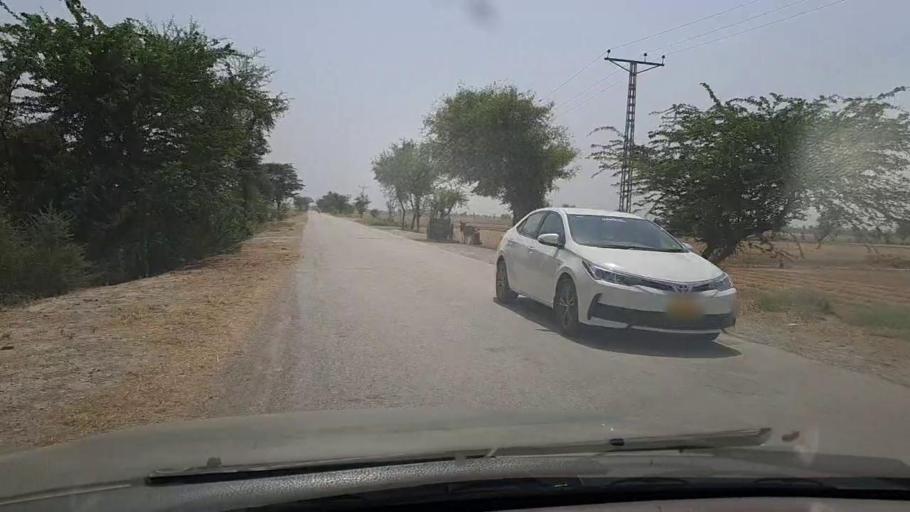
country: PK
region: Sindh
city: Miro Khan
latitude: 27.7037
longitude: 68.0621
